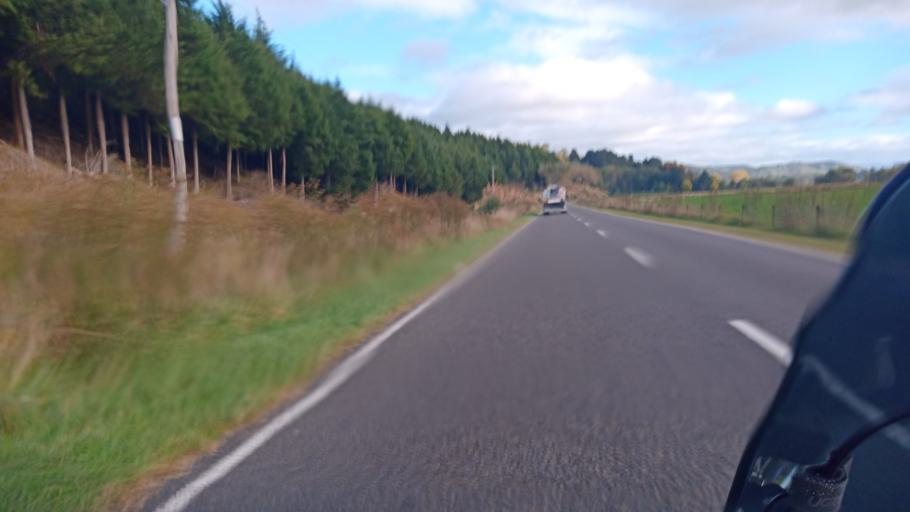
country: NZ
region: Gisborne
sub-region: Gisborne District
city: Gisborne
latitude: -38.6044
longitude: 177.8080
